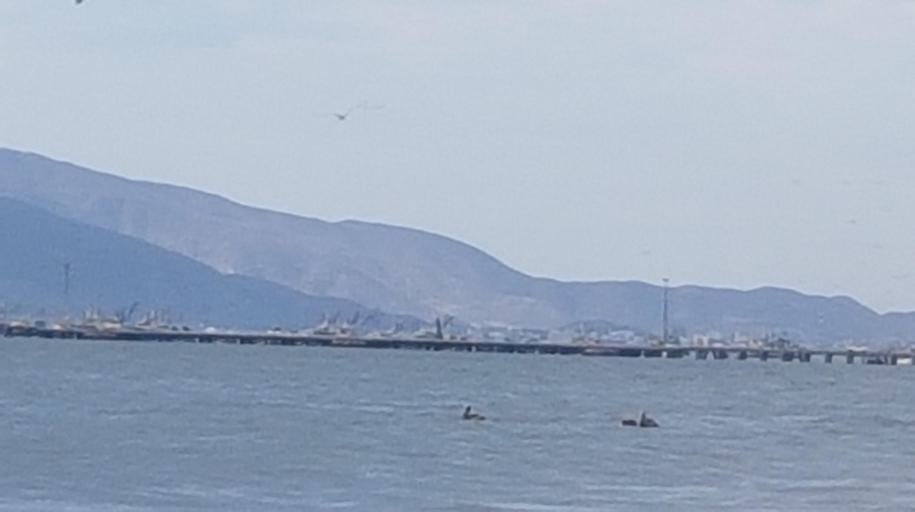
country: PE
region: Ancash
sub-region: Provincia de Santa
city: Chimbote
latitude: -9.1336
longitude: -78.5594
